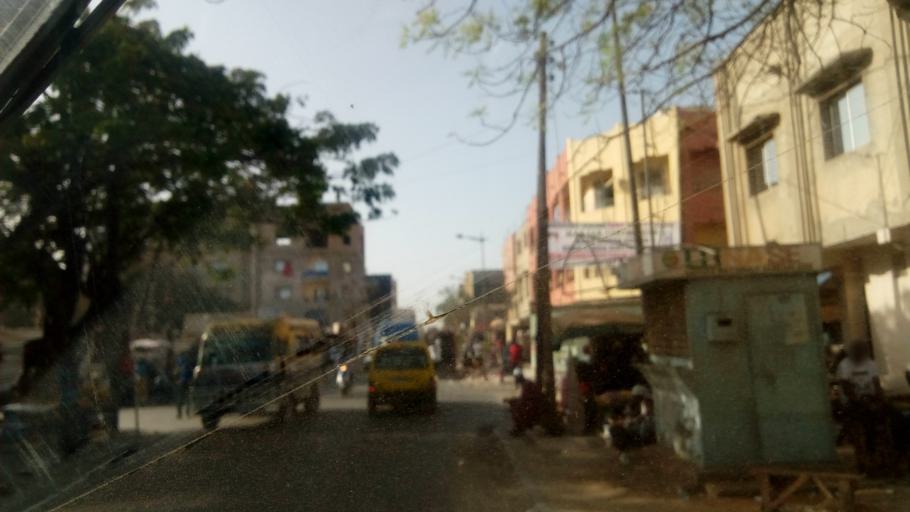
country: SN
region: Dakar
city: Dakar
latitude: 14.6833
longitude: -17.4474
